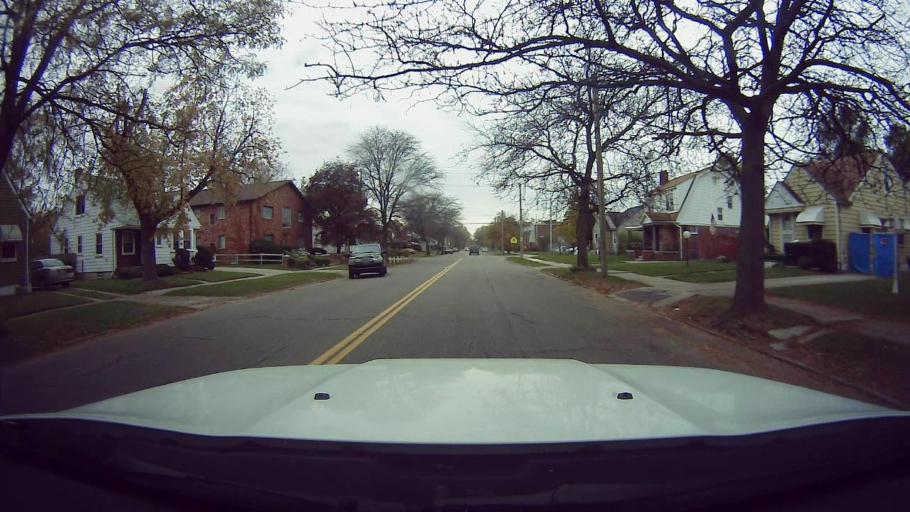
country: US
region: Michigan
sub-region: Oakland County
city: Oak Park
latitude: 42.4079
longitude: -83.1892
